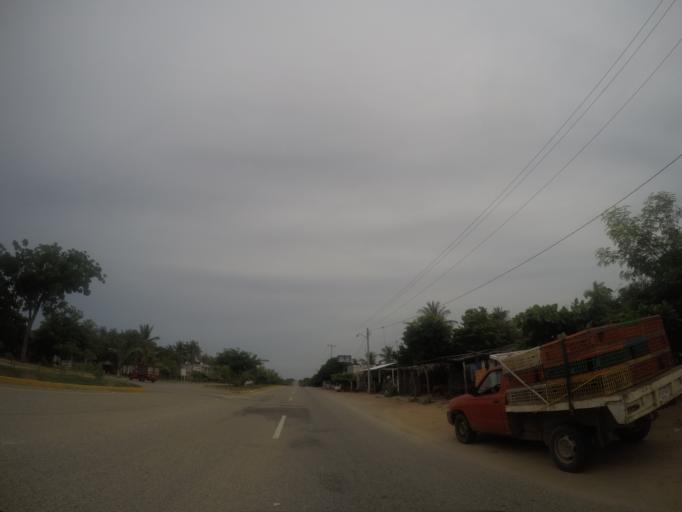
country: MX
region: Oaxaca
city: Santa Maria Colotepec
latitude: 15.7898
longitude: -96.9187
